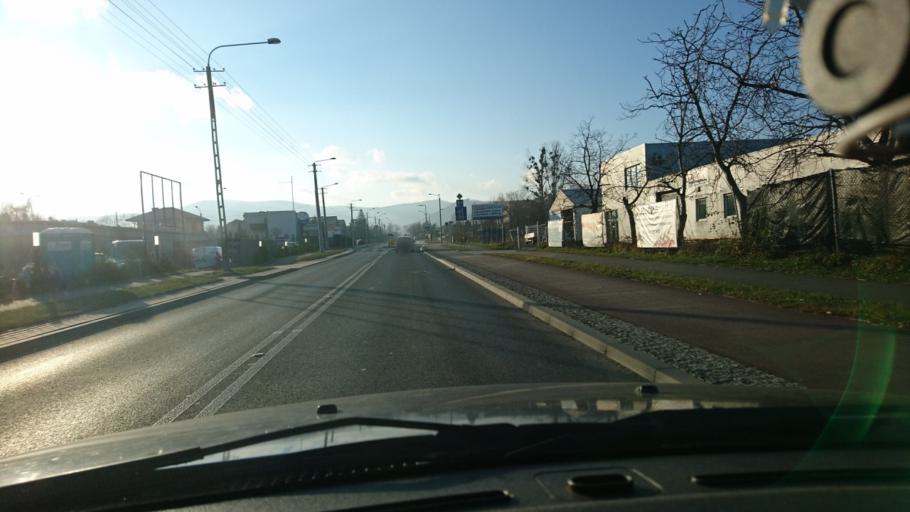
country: PL
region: Silesian Voivodeship
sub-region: Powiat bielski
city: Jaworze
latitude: 49.8190
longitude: 18.9753
